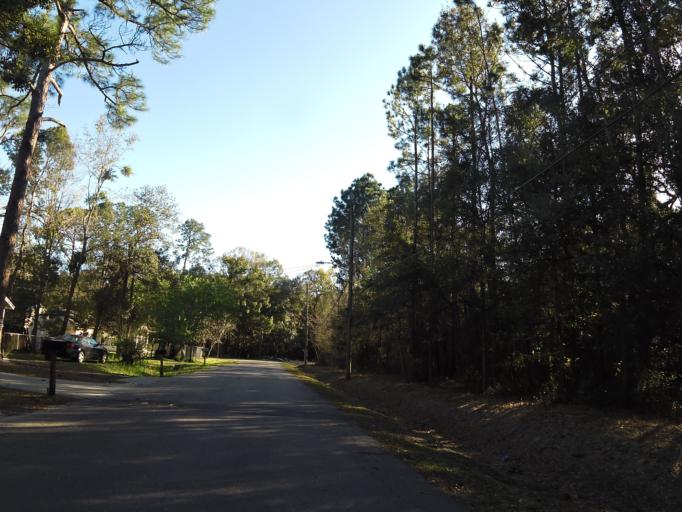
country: US
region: Florida
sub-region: Duval County
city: Jacksonville
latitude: 30.2792
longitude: -81.6327
